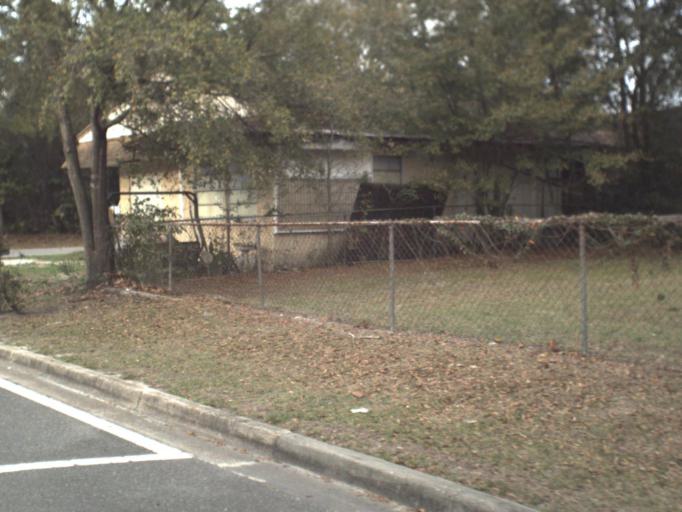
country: US
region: Florida
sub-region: Bay County
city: Cedar Grove
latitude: 30.1583
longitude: -85.6251
